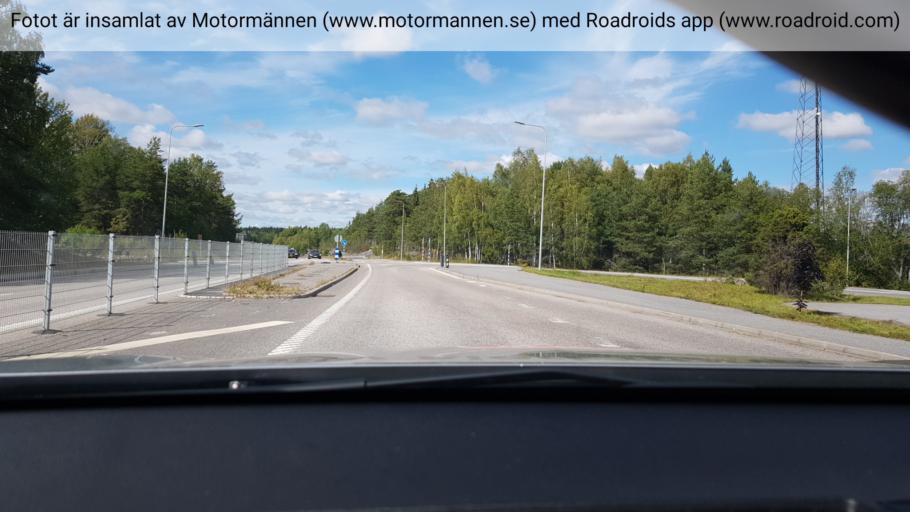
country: SE
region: Stockholm
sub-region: Osterakers Kommun
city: Akersberga
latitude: 59.4497
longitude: 18.2168
